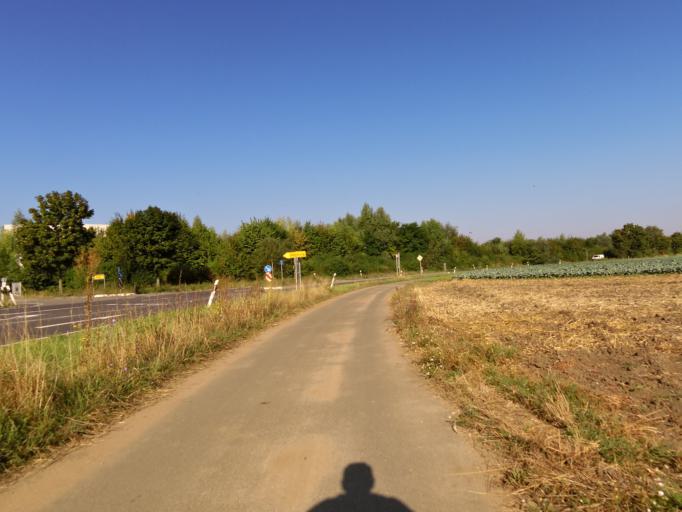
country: DE
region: Rheinland-Pfalz
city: Maxdorf
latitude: 49.4881
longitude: 8.2964
